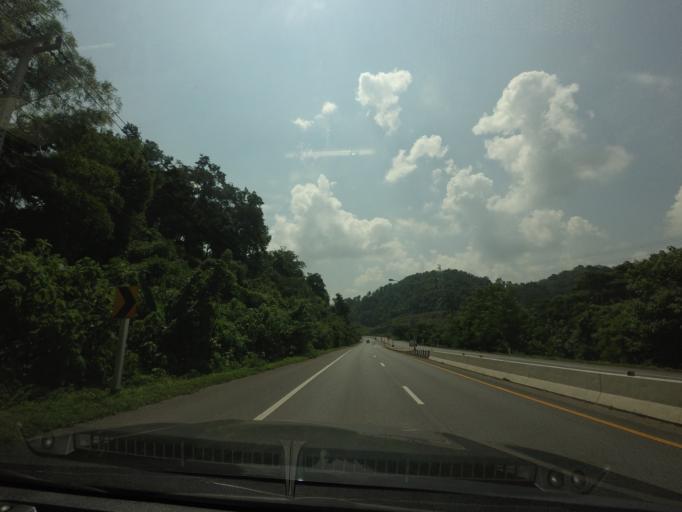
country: TH
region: Uttaradit
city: Uttaradit
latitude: 17.7732
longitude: 100.1316
